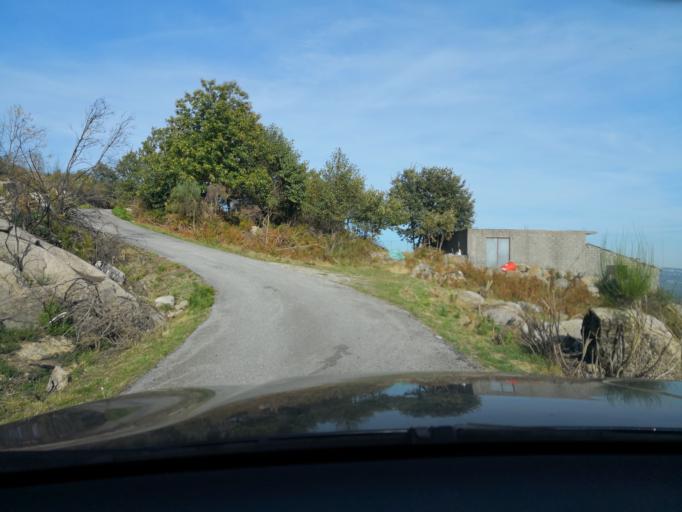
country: PT
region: Vila Real
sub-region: Vila Real
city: Vila Real
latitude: 41.3438
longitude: -7.7588
